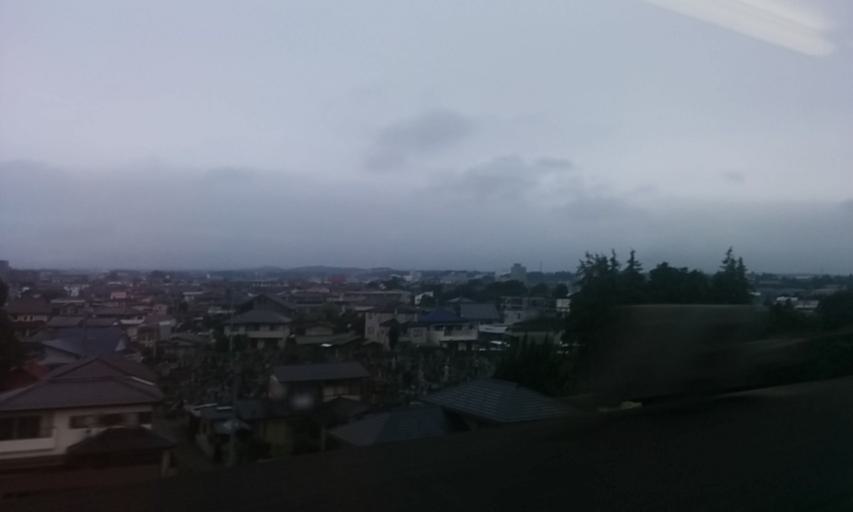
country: JP
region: Tochigi
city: Otawara
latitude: 36.8870
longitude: 139.9884
